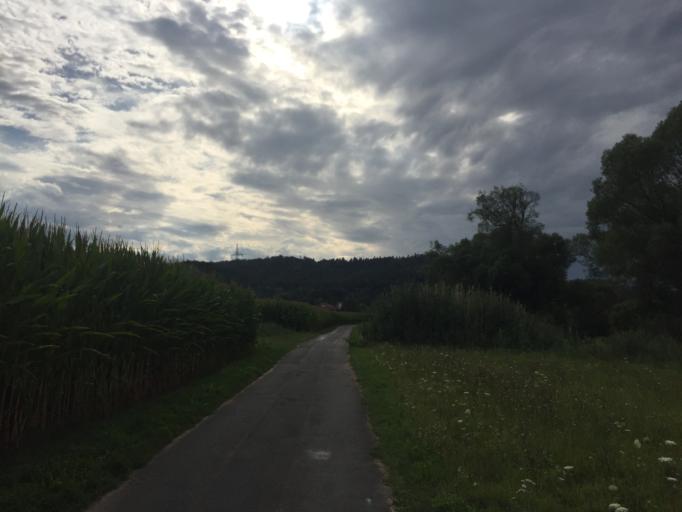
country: DE
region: Hesse
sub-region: Regierungsbezirk Kassel
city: Rotenburg an der Fulda
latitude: 51.0056
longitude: 9.6995
